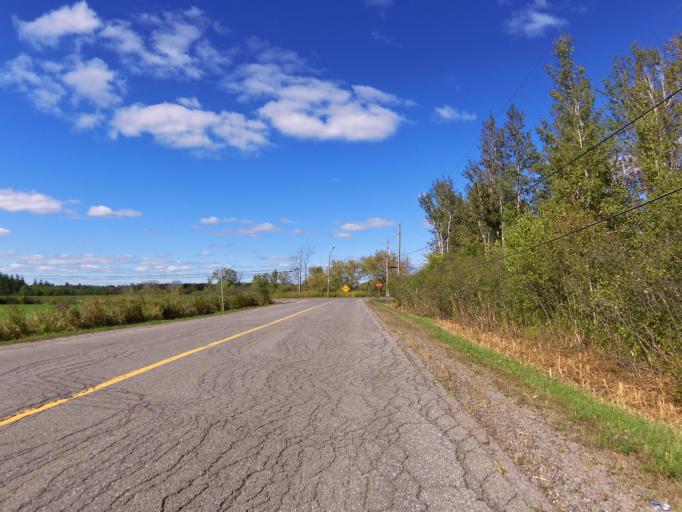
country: CA
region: Ontario
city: Ottawa
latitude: 45.3337
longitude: -75.4927
